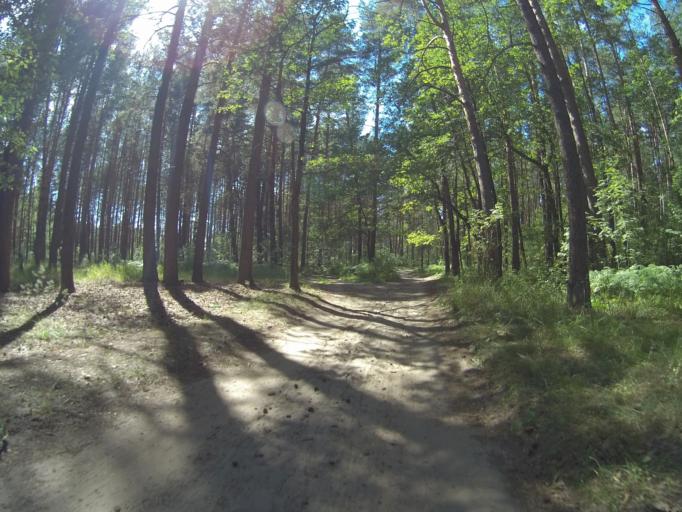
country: RU
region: Vladimir
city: Raduzhnyy
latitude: 56.0566
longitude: 40.3579
